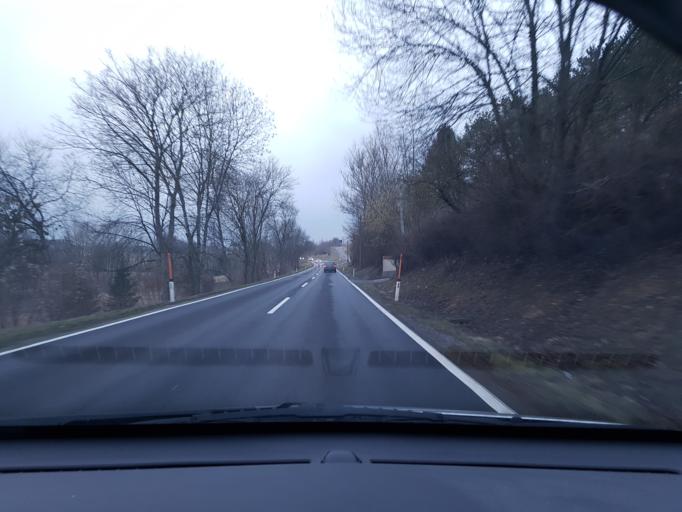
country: AT
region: Upper Austria
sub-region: Politischer Bezirk Linz-Land
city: Ansfelden
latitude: 48.1391
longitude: 14.3279
